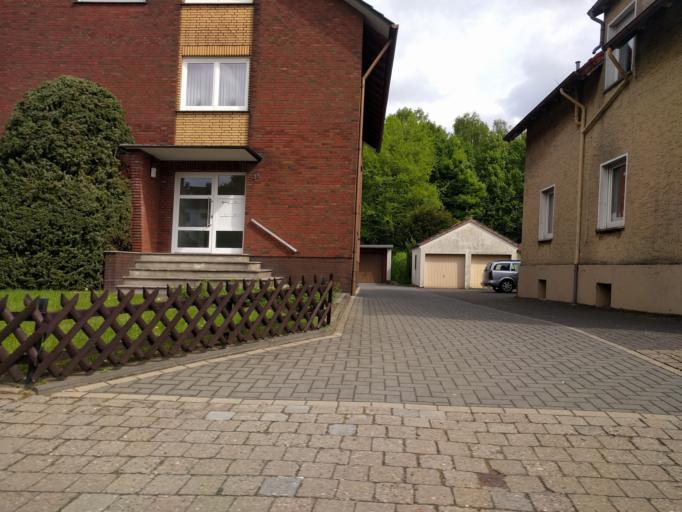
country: DE
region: North Rhine-Westphalia
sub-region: Regierungsbezirk Detmold
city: Bielefeld
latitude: 52.0560
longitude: 8.5577
